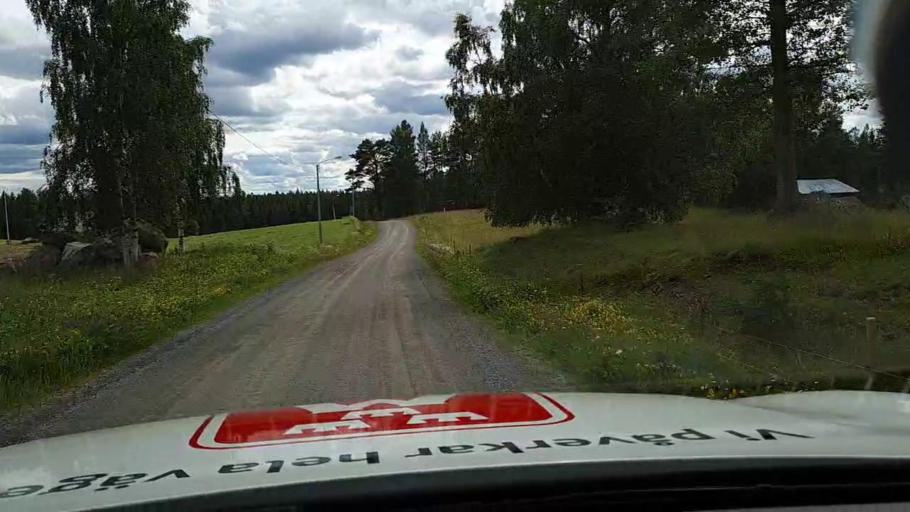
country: SE
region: Jaemtland
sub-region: Braecke Kommun
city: Braecke
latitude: 63.2819
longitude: 15.3712
